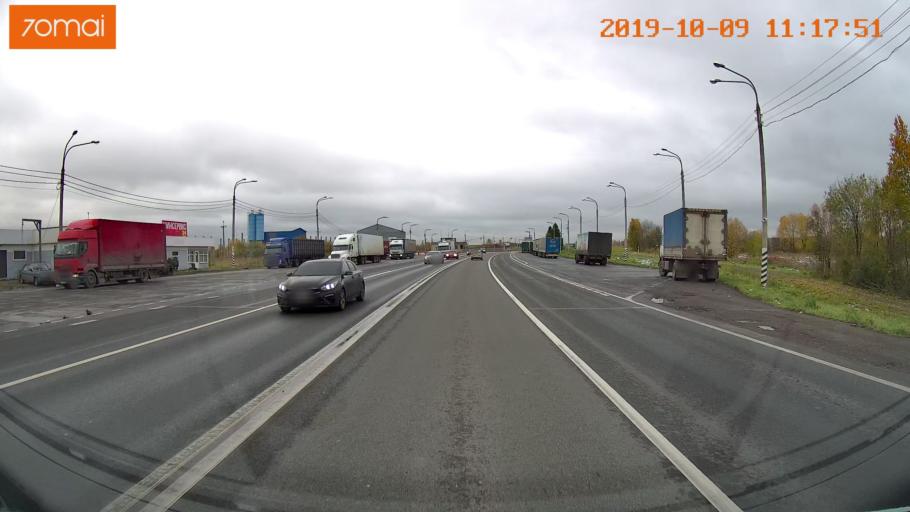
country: RU
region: Vologda
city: Vologda
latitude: 59.1721
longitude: 39.9057
